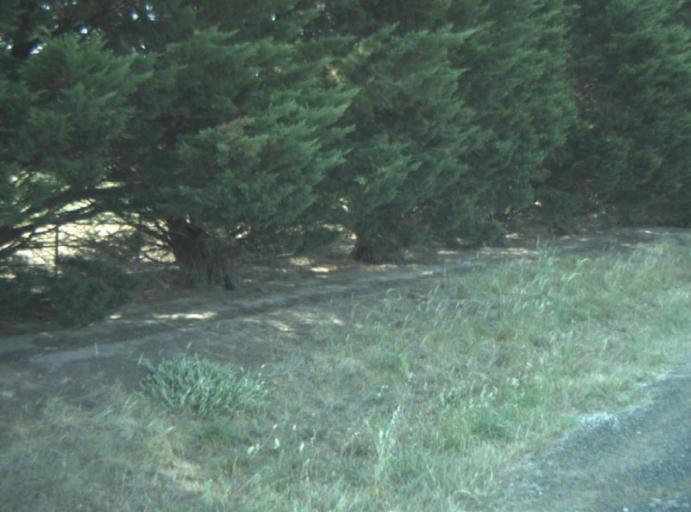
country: AU
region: Victoria
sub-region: Greater Geelong
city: Leopold
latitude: -38.1910
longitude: 144.5110
